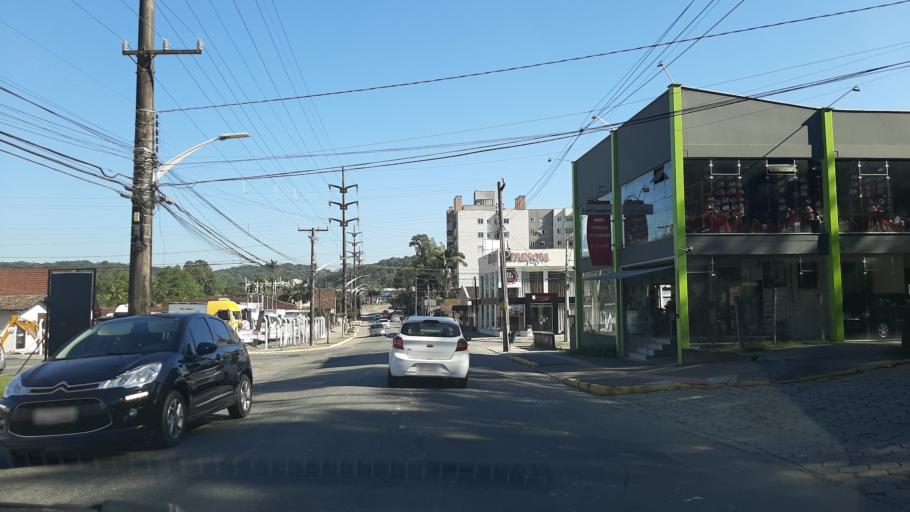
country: BR
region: Santa Catarina
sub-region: Joinville
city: Joinville
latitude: -26.3188
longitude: -48.8678
